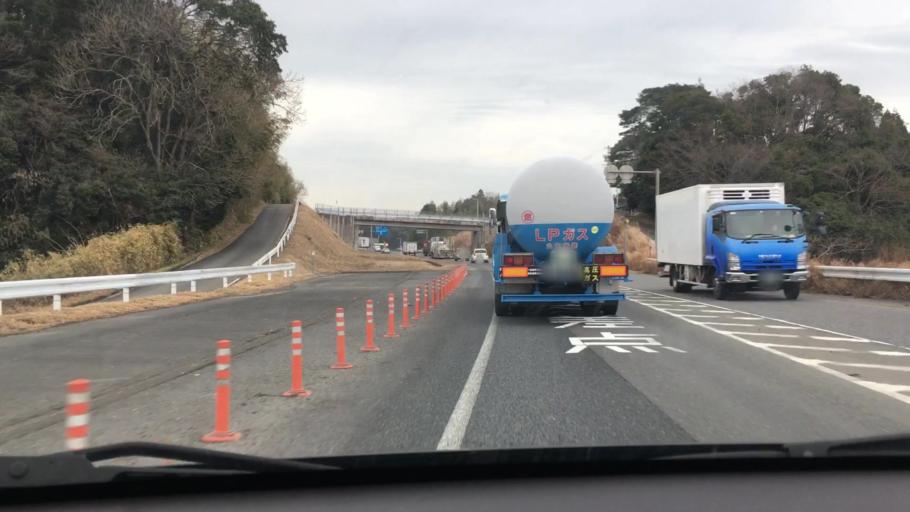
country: JP
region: Mie
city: Kameyama
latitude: 34.8616
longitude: 136.4607
